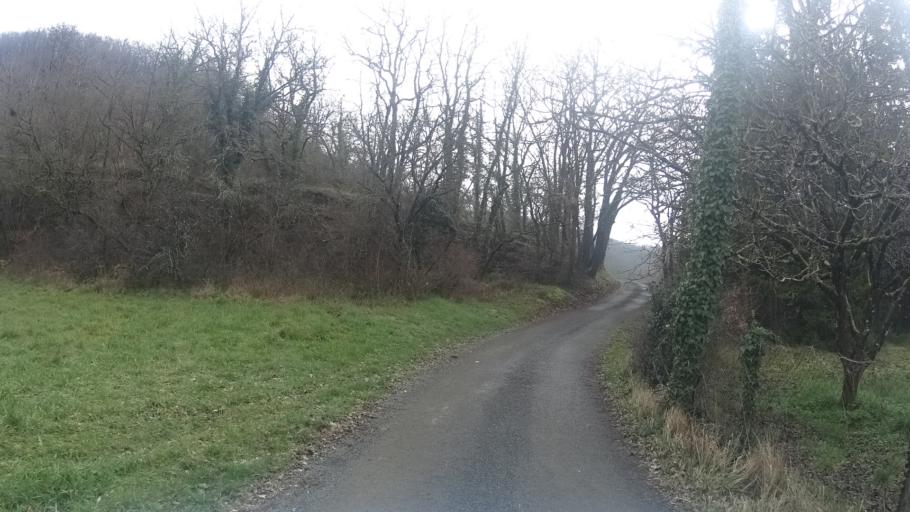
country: FR
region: Aquitaine
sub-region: Departement de la Dordogne
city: Terrasson-Lavilledieu
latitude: 45.1102
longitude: 1.2271
